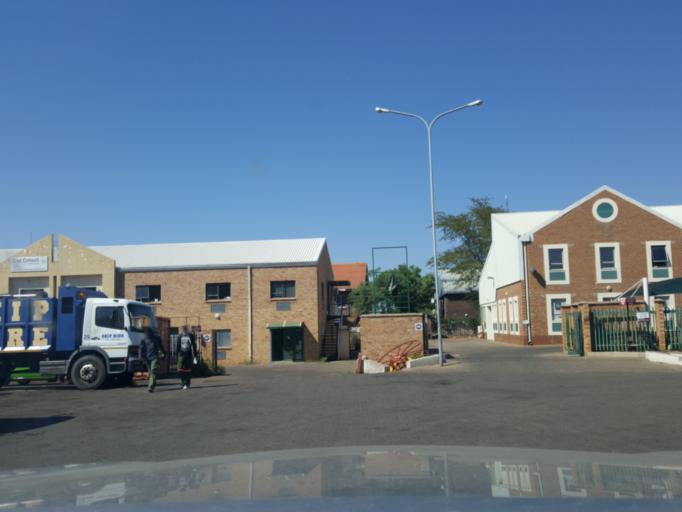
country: BW
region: South East
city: Gaborone
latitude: -24.6933
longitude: 25.8829
